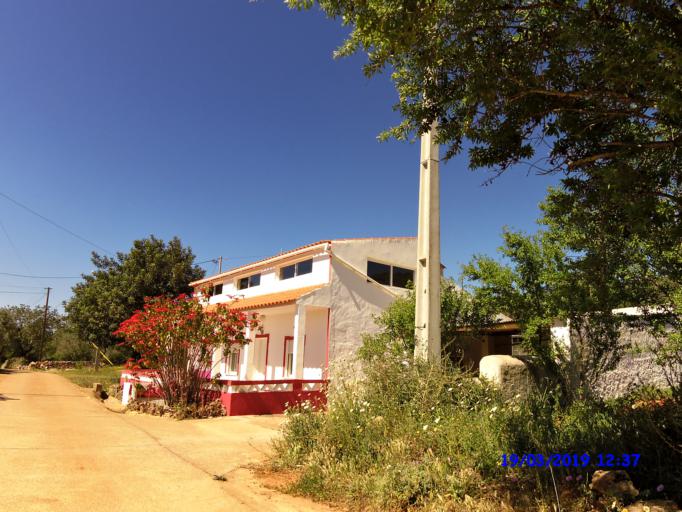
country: PT
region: Faro
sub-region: Loule
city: Boliqueime
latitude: 37.2076
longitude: -8.1604
